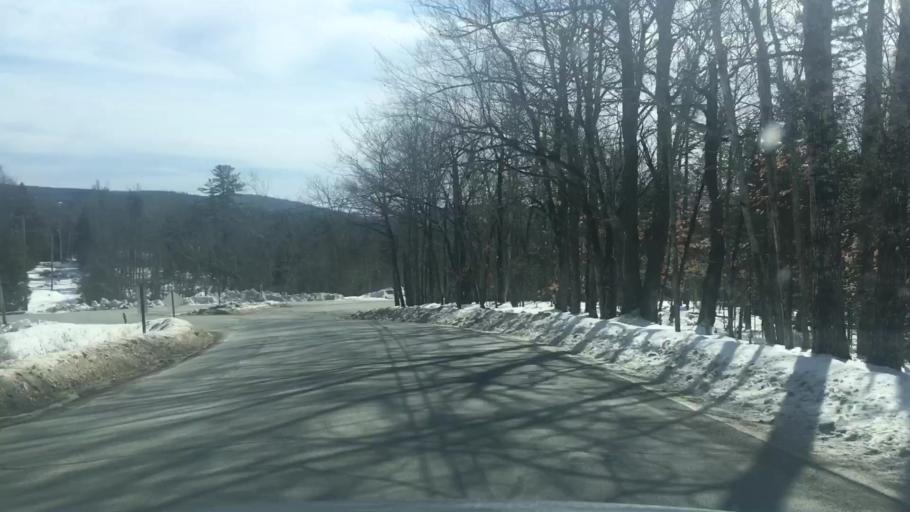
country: US
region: Maine
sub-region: Penobscot County
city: Holden
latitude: 44.7597
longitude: -68.6414
